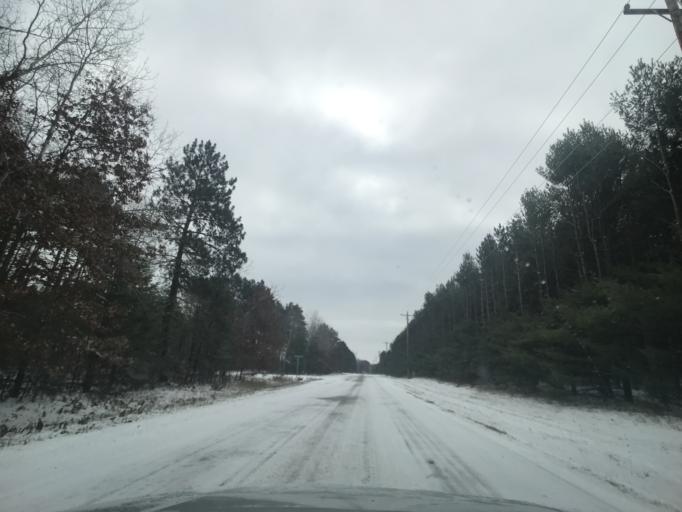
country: US
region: Wisconsin
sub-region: Brown County
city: Suamico
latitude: 44.6972
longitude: -88.1009
